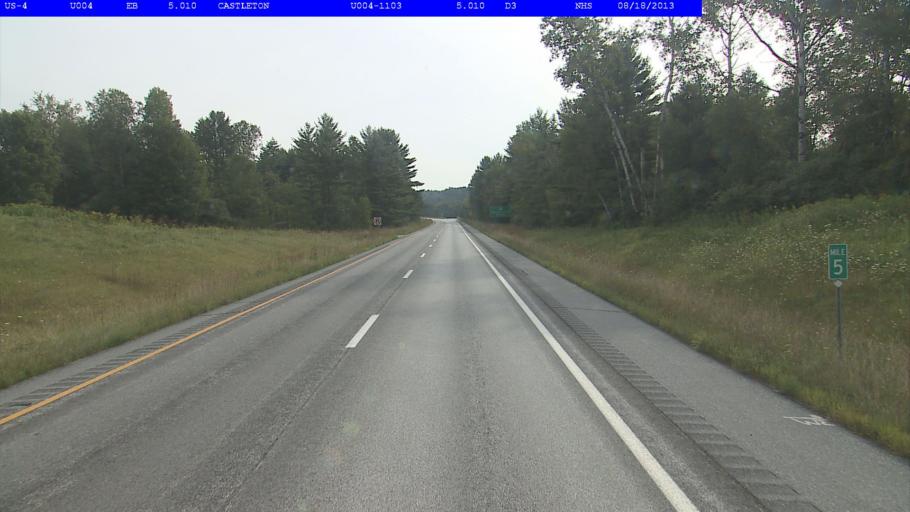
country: US
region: Vermont
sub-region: Rutland County
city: Castleton
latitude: 43.6141
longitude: -73.2149
